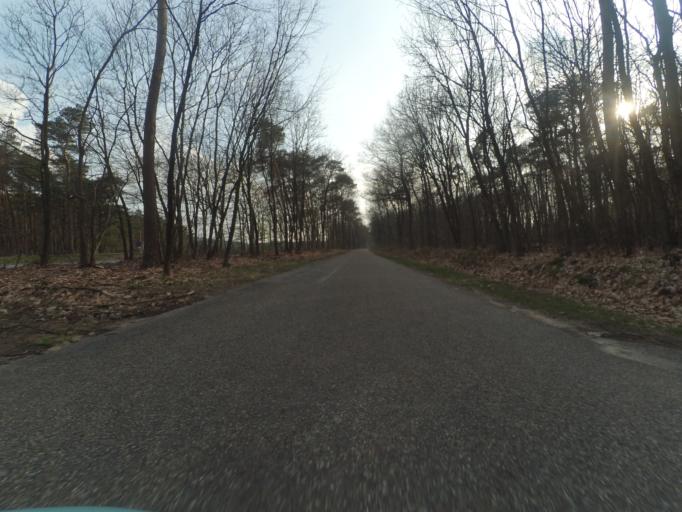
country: NL
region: Gelderland
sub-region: Gemeente Apeldoorn
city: Beekbergen
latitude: 52.1687
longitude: 5.9057
